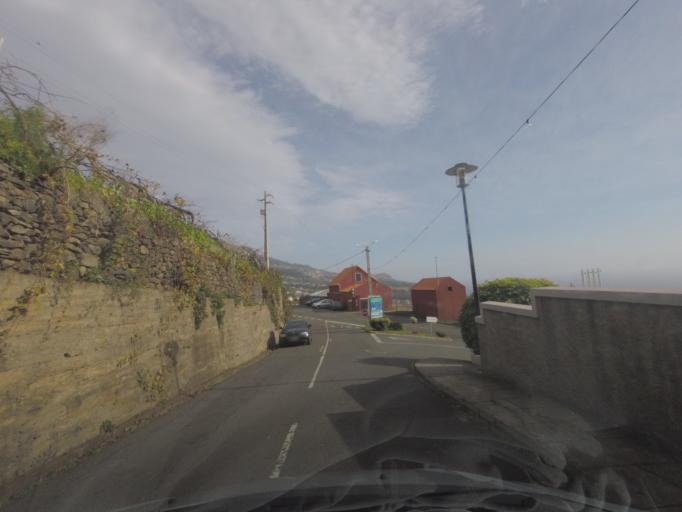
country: PT
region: Madeira
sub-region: Calheta
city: Estreito da Calheta
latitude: 32.7358
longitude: -17.1875
